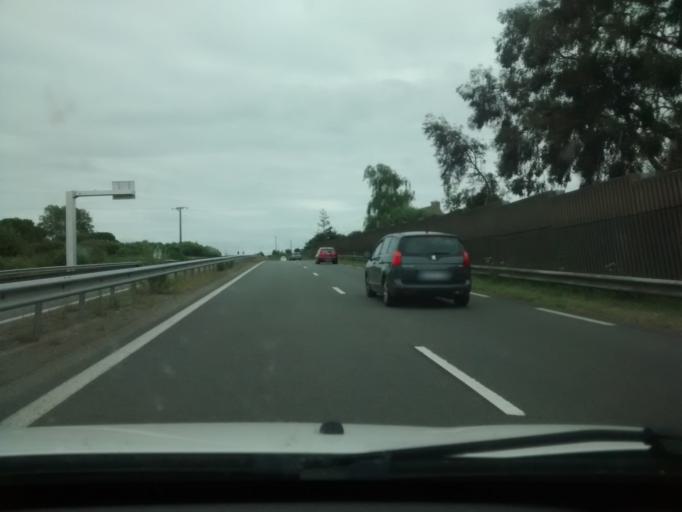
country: FR
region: Brittany
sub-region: Departement des Cotes-d'Armor
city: Rospez
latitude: 48.7179
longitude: -3.4111
